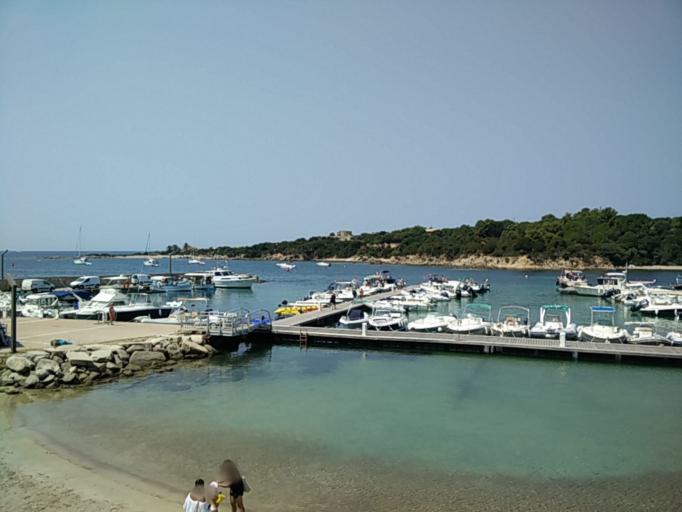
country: FR
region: Corsica
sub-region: Departement de la Corse-du-Sud
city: Propriano
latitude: 41.5424
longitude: 8.8516
